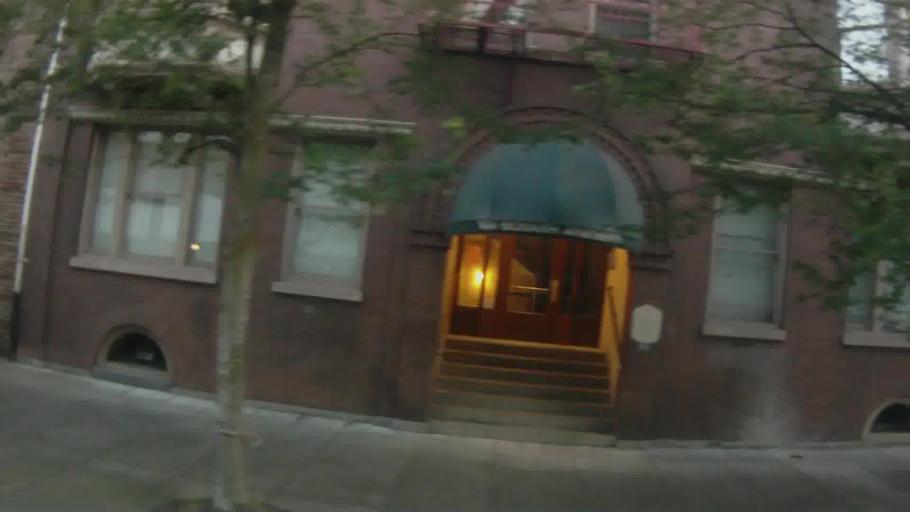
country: US
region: Oregon
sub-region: Multnomah County
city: Portland
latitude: 45.5213
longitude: -122.6868
